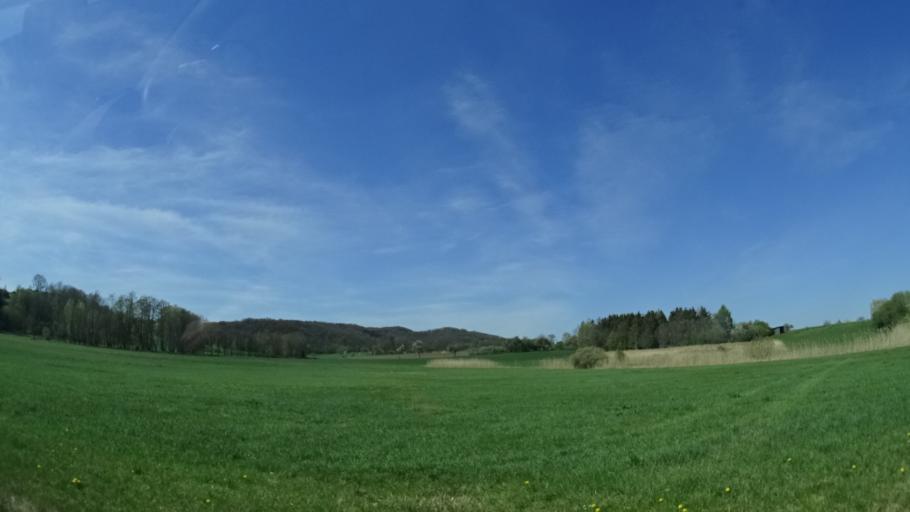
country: DE
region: Thuringia
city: Veilsdorf
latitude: 50.3029
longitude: 10.7979
